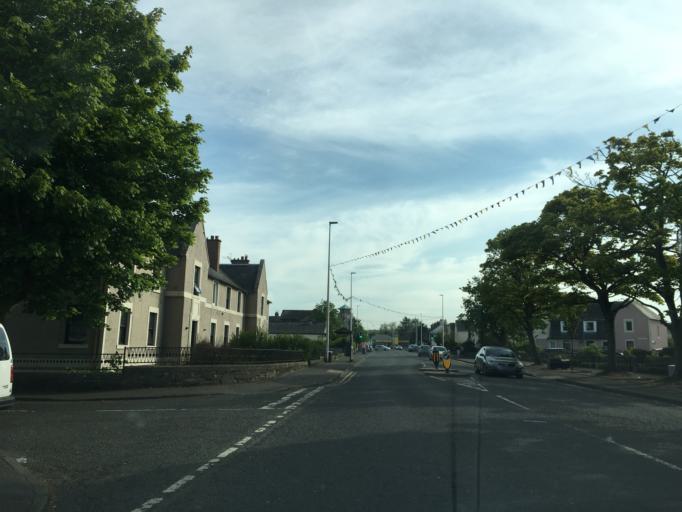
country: GB
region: Scotland
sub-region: Midlothian
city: Penicuik
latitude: 55.8338
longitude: -3.2222
